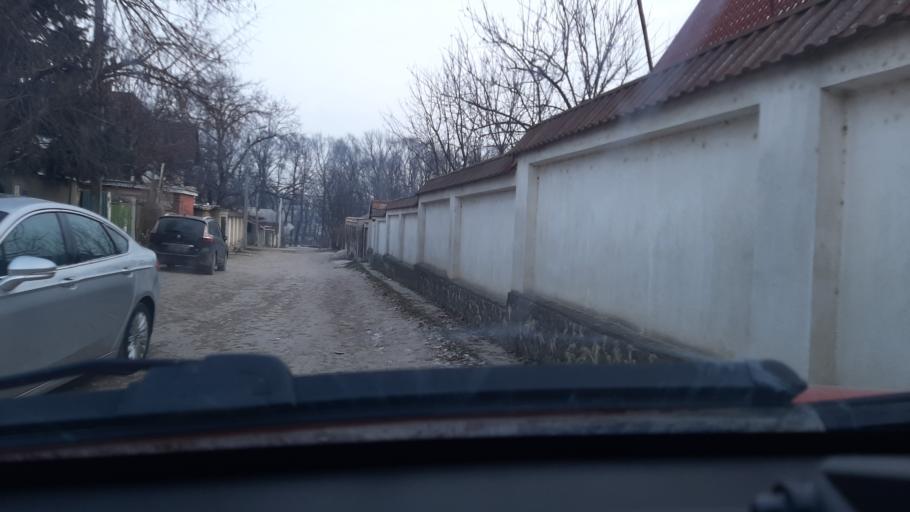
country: MD
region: Chisinau
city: Chisinau
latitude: 46.9856
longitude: 28.8938
